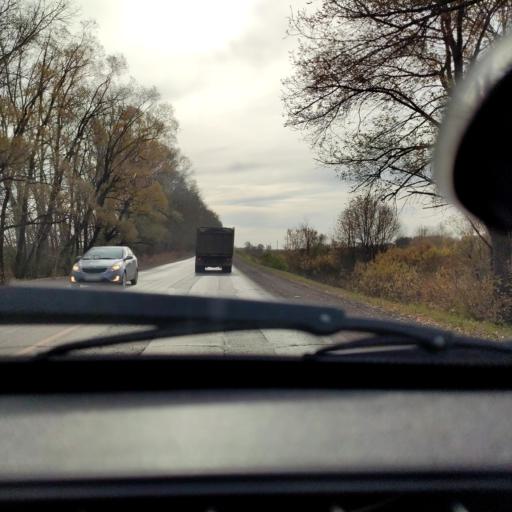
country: RU
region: Bashkortostan
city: Avdon
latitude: 54.7330
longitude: 55.8040
